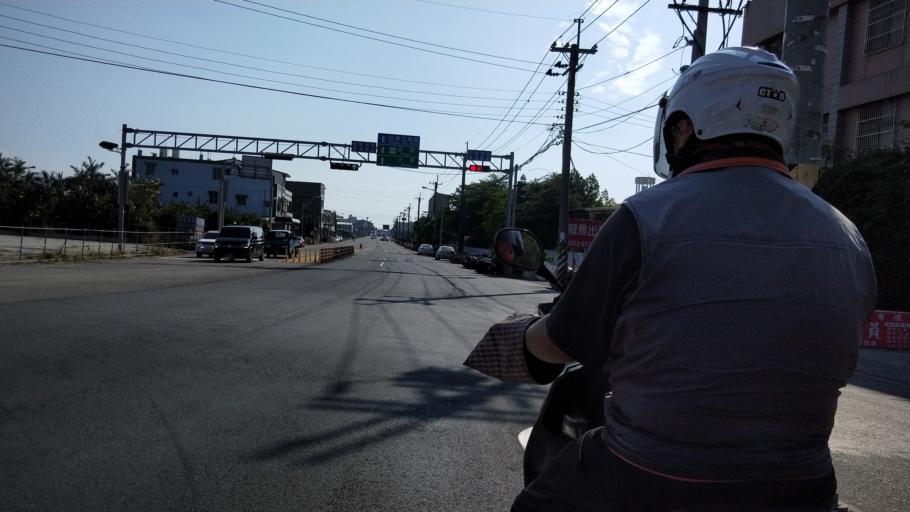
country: TW
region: Taiwan
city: Fengyuan
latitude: 24.3961
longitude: 120.6578
